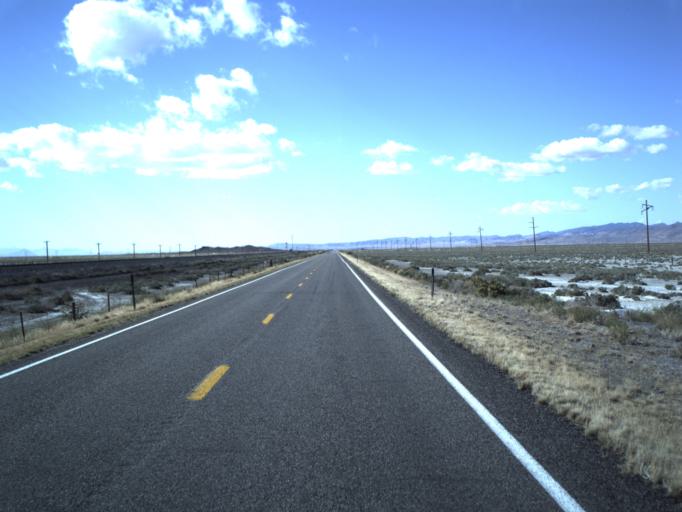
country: US
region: Utah
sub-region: Millard County
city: Delta
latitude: 39.1741
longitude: -112.7042
